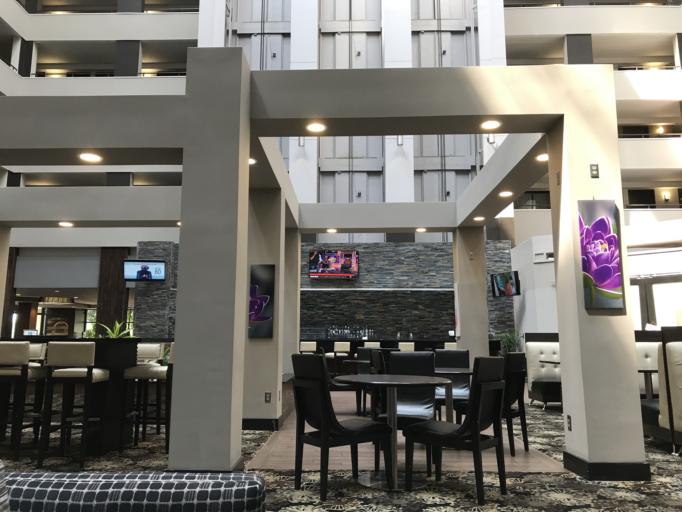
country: US
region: Michigan
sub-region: Oakland County
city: Franklin
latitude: 42.4947
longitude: -83.2992
